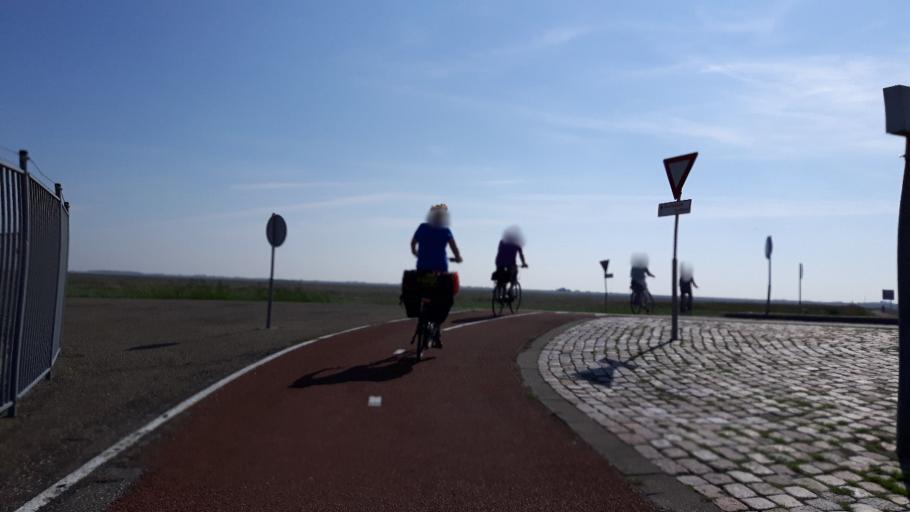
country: NL
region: Friesland
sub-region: Gemeente Dongeradeel
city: Holwerd
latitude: 53.3918
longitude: 5.8828
